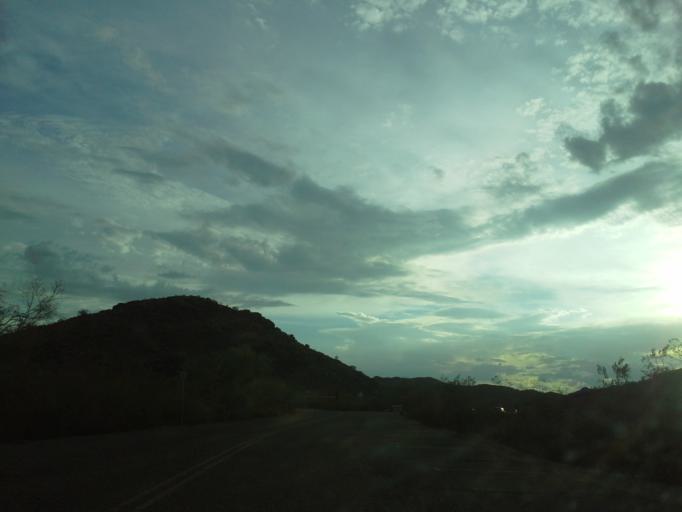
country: US
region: Arizona
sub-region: Maricopa County
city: Guadalupe
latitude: 33.3632
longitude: -111.9829
